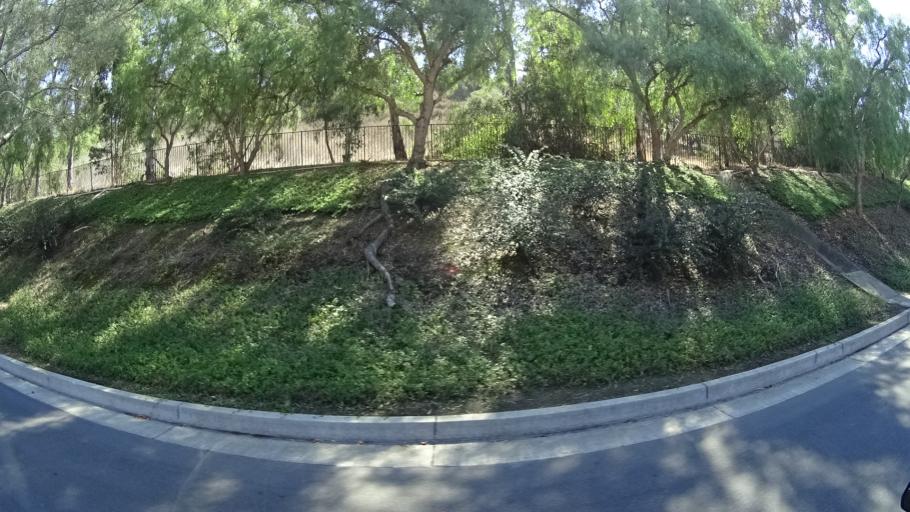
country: US
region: California
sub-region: Orange County
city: San Clemente
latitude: 33.4611
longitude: -117.6257
